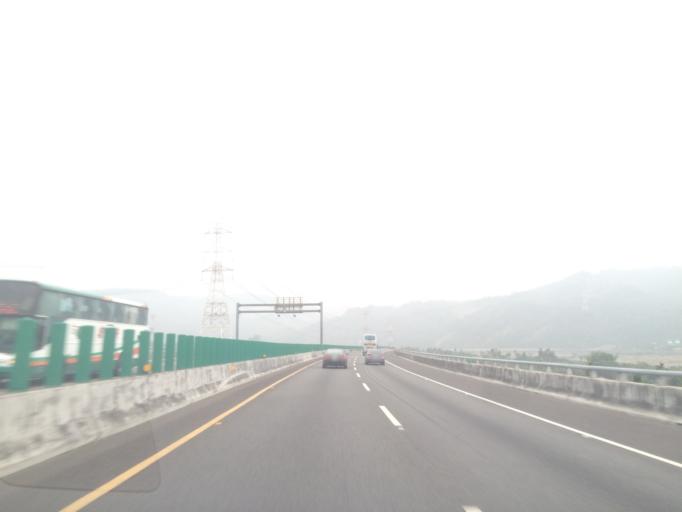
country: TW
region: Taiwan
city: Zhongxing New Village
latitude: 23.9930
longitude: 120.7518
